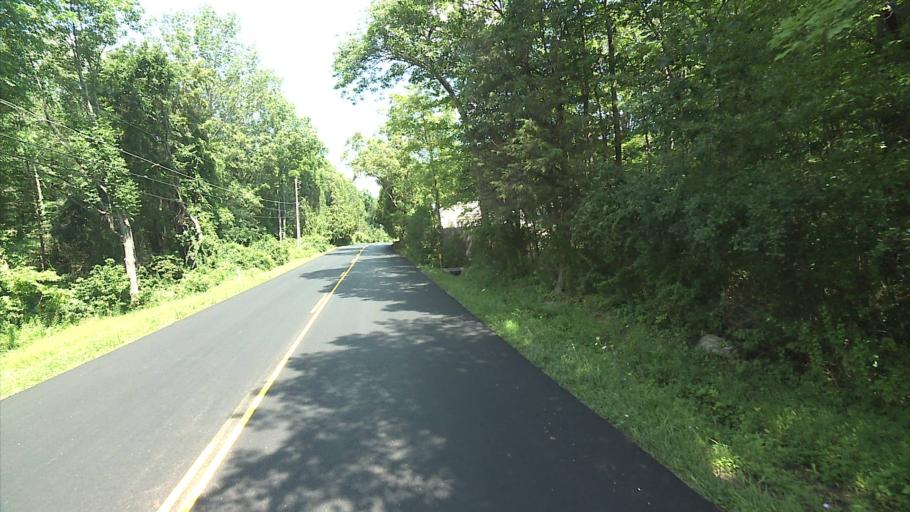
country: US
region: Connecticut
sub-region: Litchfield County
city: Canaan
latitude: 41.9920
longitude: -73.3611
